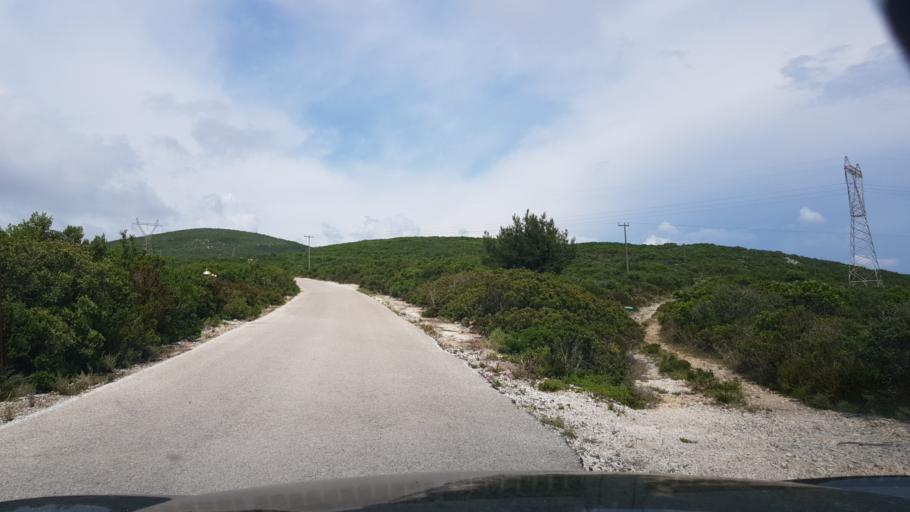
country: GR
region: Ionian Islands
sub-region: Lefkada
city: Nidri
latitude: 38.5983
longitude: 20.5567
